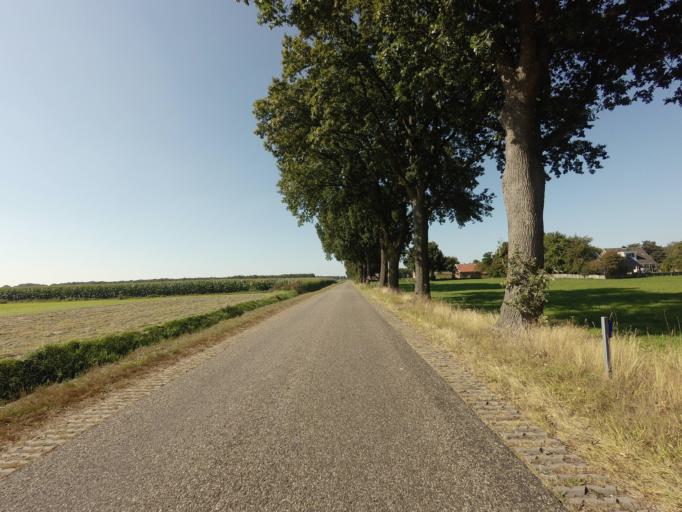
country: DE
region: Lower Saxony
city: Wielen
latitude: 52.5227
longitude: 6.6589
